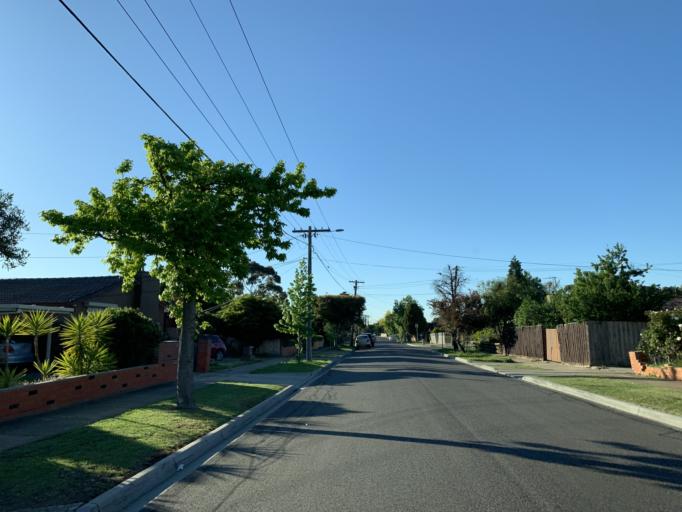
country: AU
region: Victoria
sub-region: Brimbank
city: St Albans
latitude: -37.7537
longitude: 144.8082
